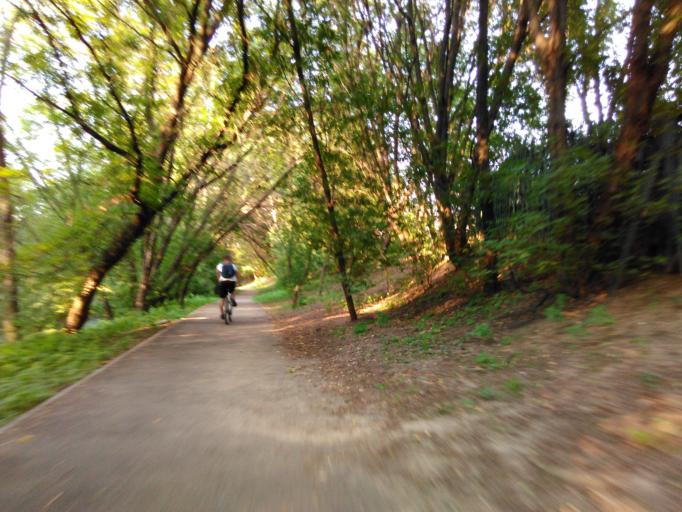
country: RU
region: Moscow
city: Vorob'yovo
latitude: 55.7241
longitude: 37.5177
